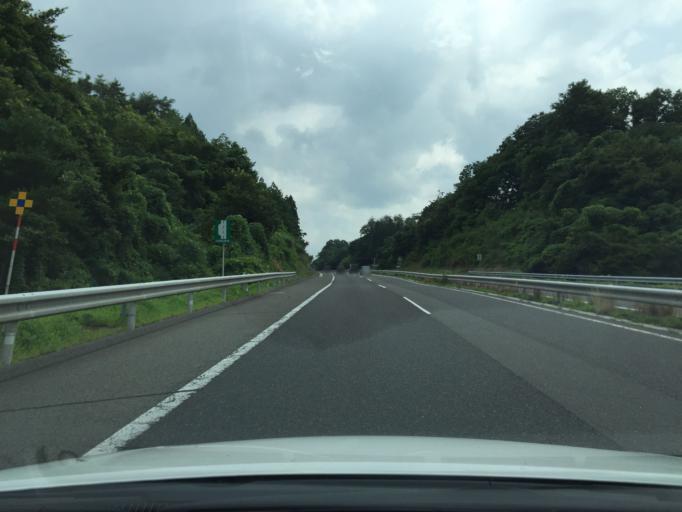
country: JP
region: Fukushima
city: Funehikimachi-funehiki
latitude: 37.3784
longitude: 140.5986
